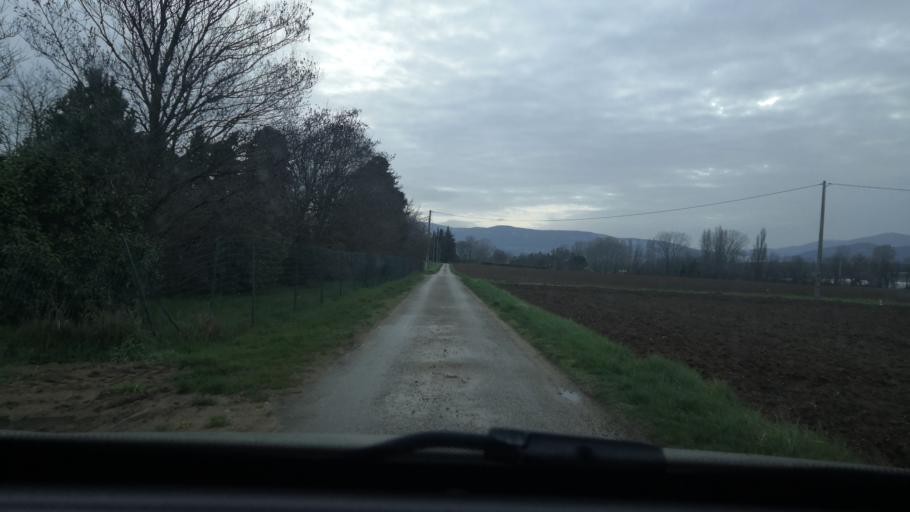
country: FR
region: Rhone-Alpes
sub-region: Departement de la Drome
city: La Begude-de-Mazenc
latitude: 44.5641
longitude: 4.8918
